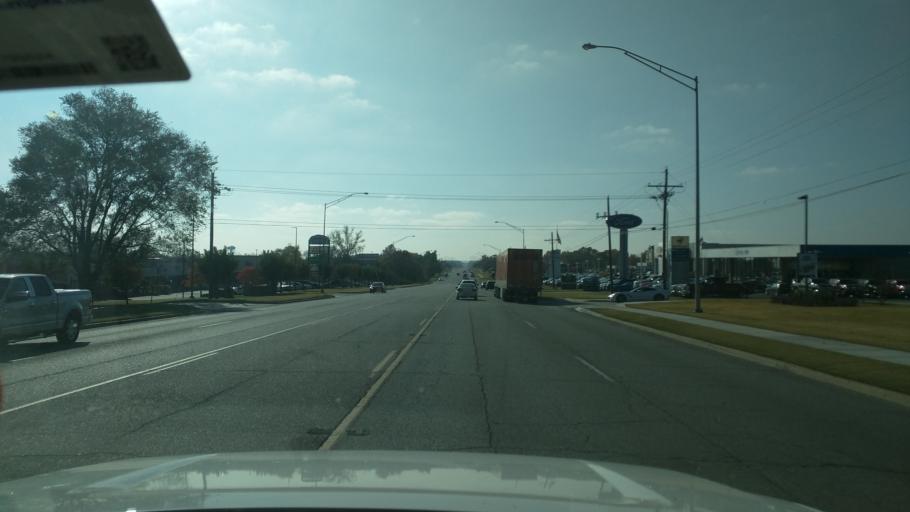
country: US
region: Oklahoma
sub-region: Washington County
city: Bartlesville
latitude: 36.7250
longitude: -95.9352
